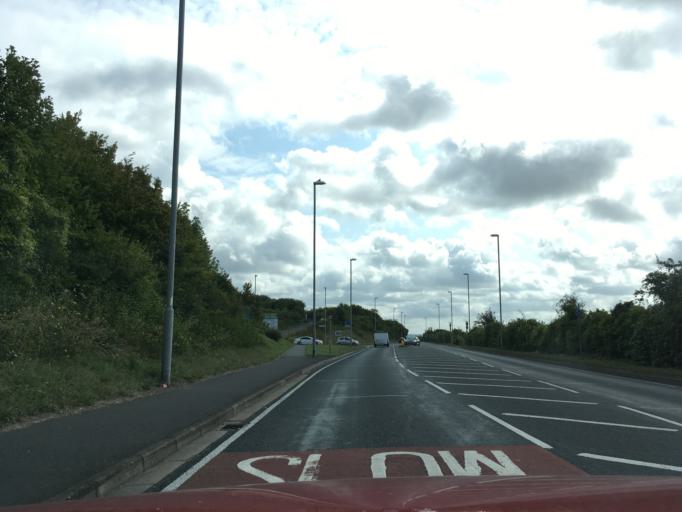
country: GB
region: England
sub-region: Portsmouth
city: Cosham
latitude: 50.8522
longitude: -1.0355
